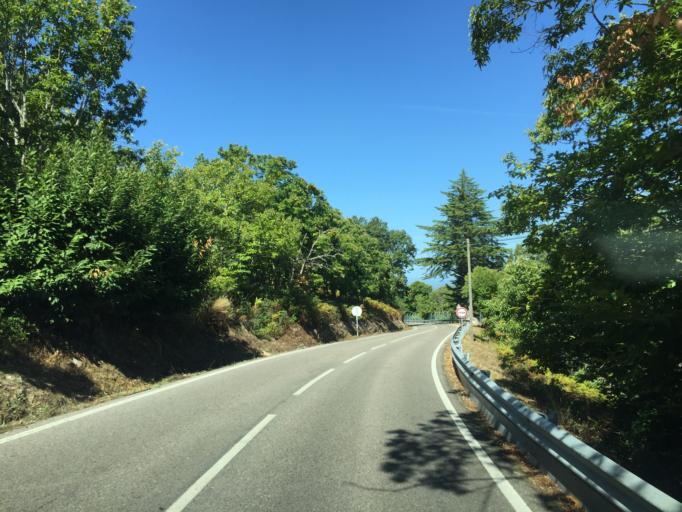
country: PT
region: Portalegre
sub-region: Marvao
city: Marvao
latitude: 39.4000
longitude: -7.3794
